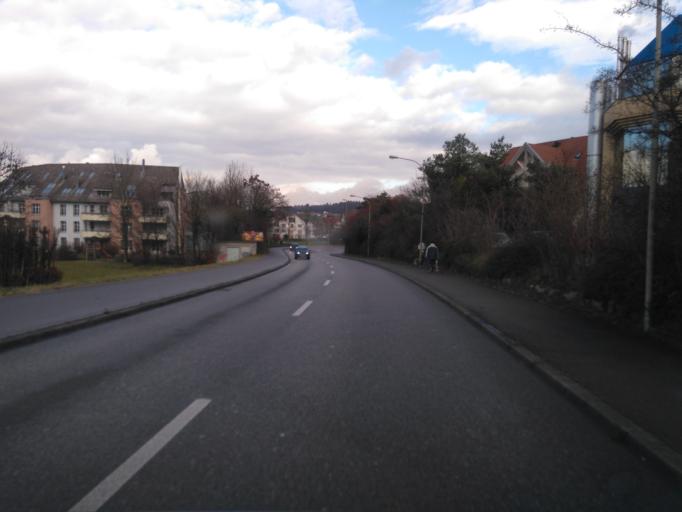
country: CH
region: Zurich
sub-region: Bezirk Dielsdorf
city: Regensdorf
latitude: 47.4386
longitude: 8.4748
